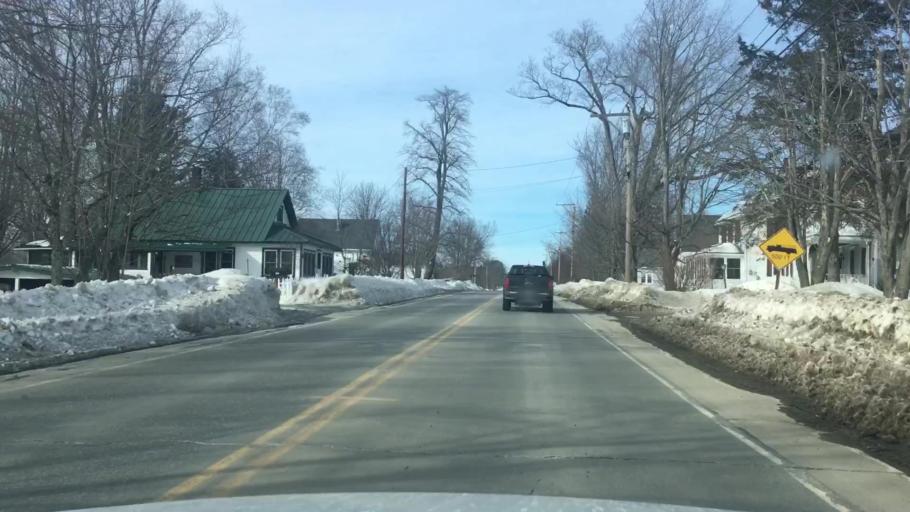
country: US
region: Maine
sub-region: Penobscot County
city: Kenduskeag
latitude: 44.9206
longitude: -68.9314
